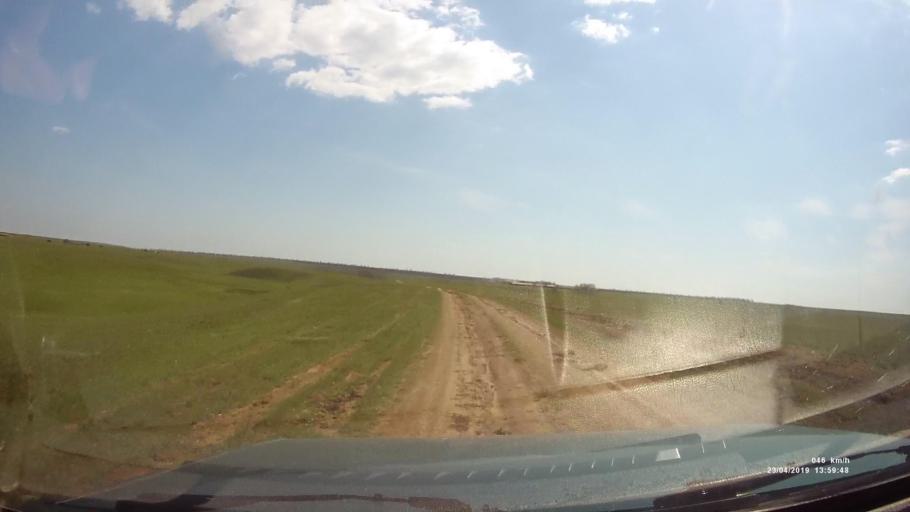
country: RU
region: Rostov
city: Remontnoye
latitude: 46.5639
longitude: 42.9469
